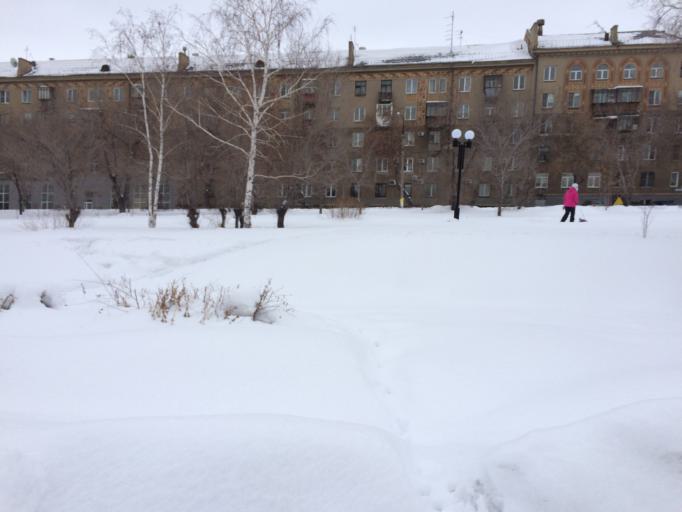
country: RU
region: Chelyabinsk
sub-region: Gorod Magnitogorsk
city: Magnitogorsk
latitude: 53.4157
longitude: 59.0019
